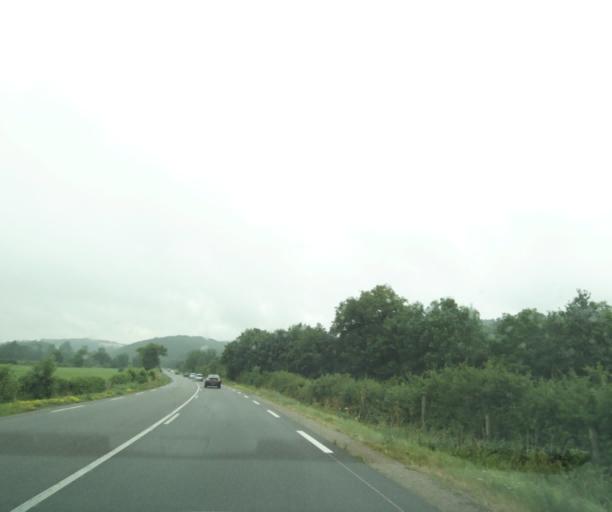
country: FR
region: Midi-Pyrenees
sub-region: Departement de l'Aveyron
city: Bozouls
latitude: 44.3997
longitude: 2.7452
